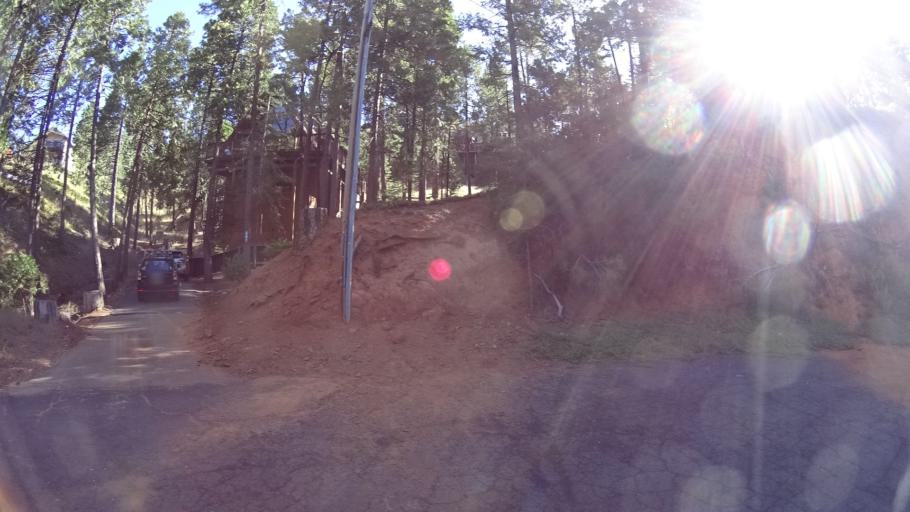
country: US
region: California
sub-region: Calaveras County
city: Arnold
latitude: 38.2607
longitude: -120.3269
